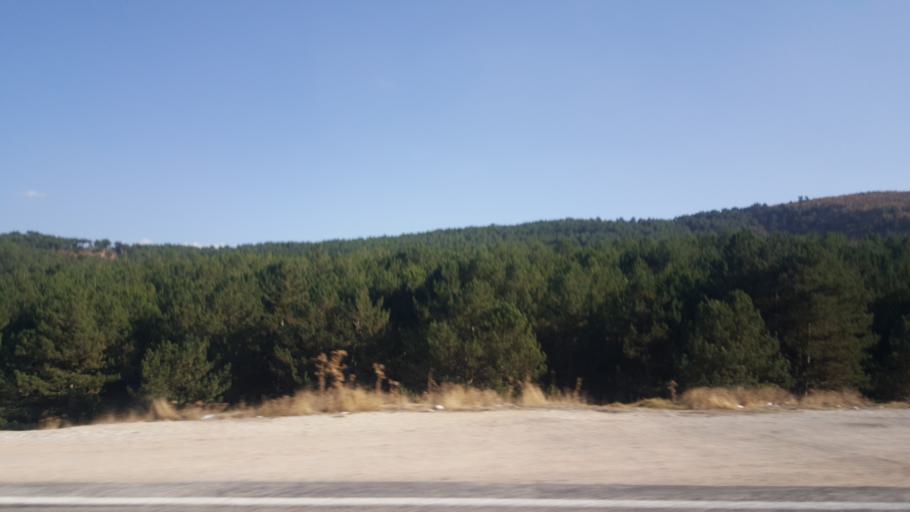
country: TR
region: Eskisehir
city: Kirka
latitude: 39.1179
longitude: 30.5891
